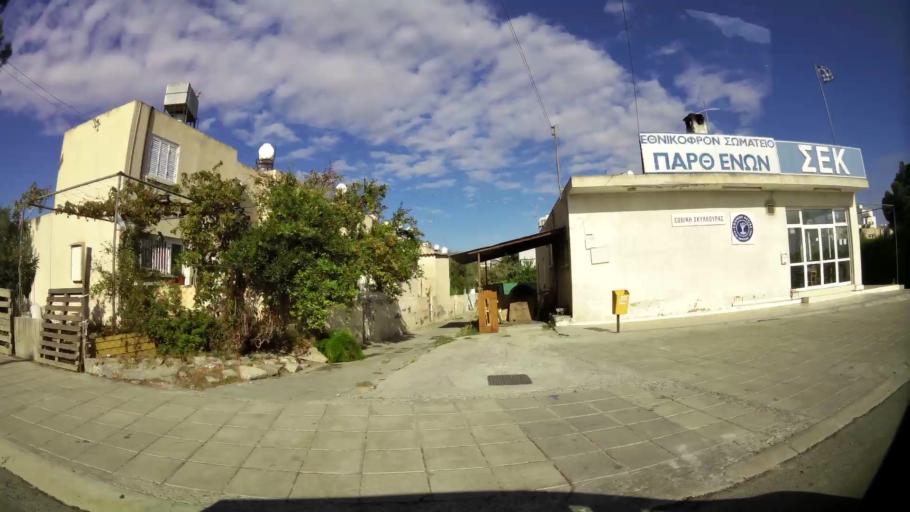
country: CY
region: Lefkosia
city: Nicosia
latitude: 35.1312
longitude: 33.3671
